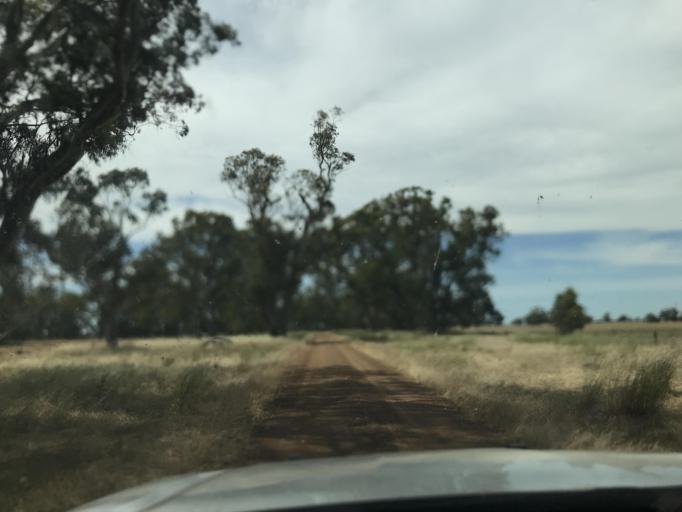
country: AU
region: South Australia
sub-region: Wattle Range
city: Penola
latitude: -37.0180
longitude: 141.4810
